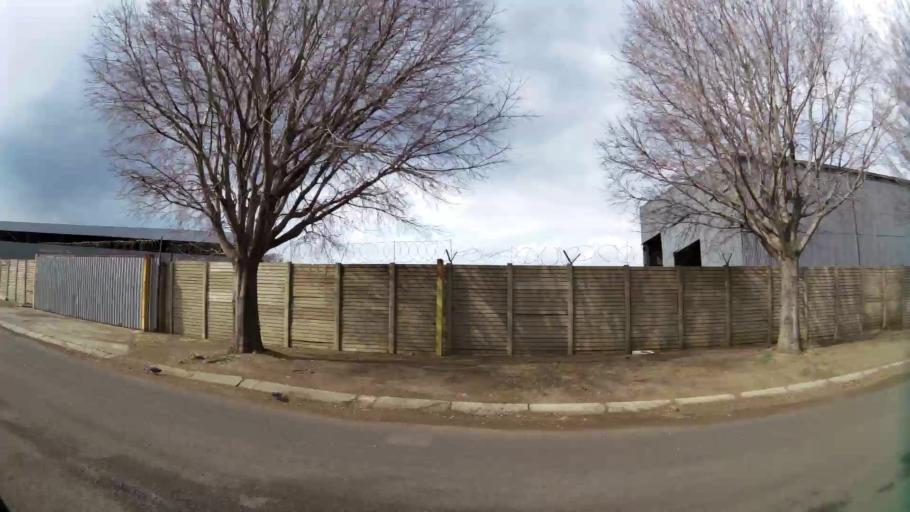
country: ZA
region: Gauteng
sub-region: Sedibeng District Municipality
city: Vanderbijlpark
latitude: -26.6879
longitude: 27.8095
